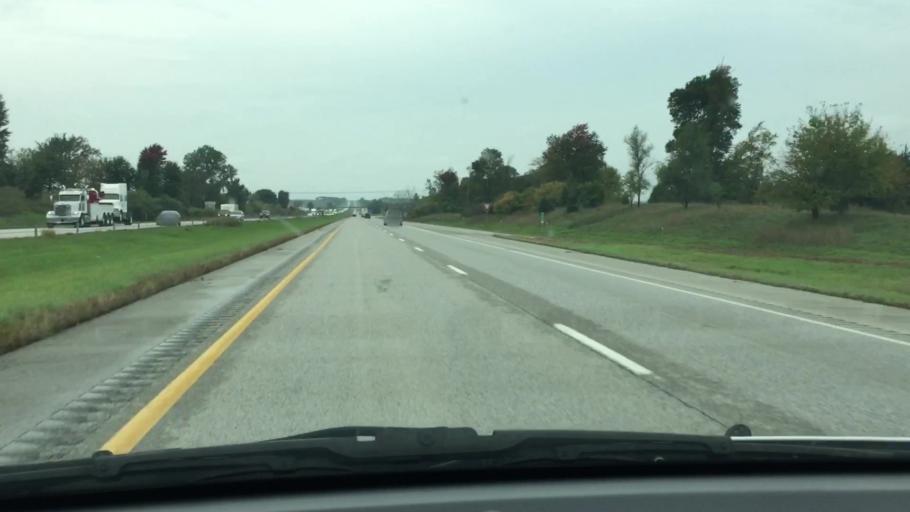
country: US
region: Iowa
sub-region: Johnson County
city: Tiffin
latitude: 41.6941
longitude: -91.6705
